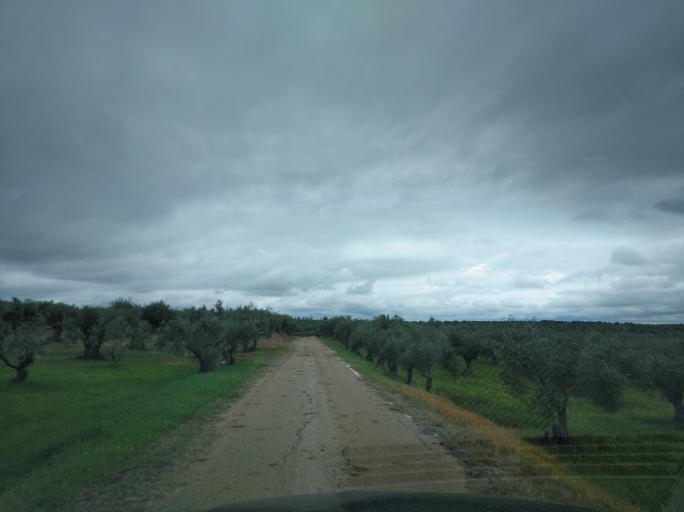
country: PT
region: Portalegre
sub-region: Campo Maior
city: Campo Maior
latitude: 38.9820
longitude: -7.0341
